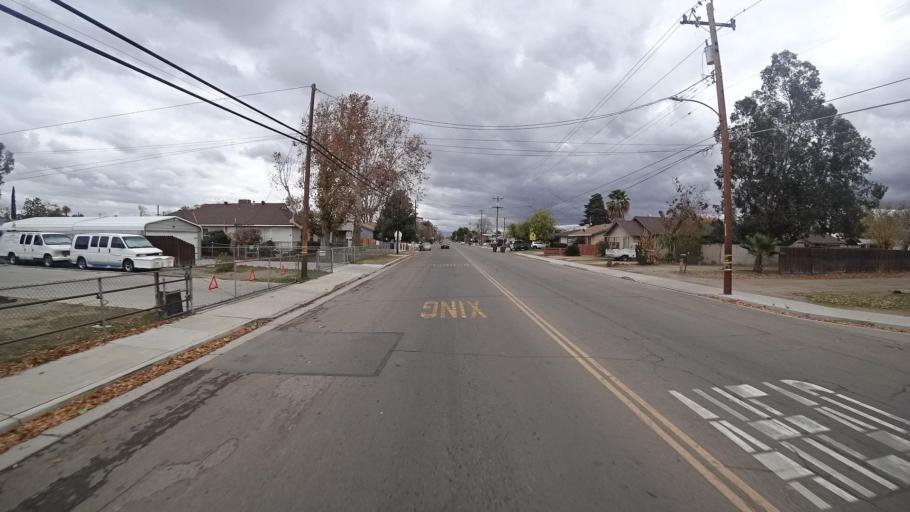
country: US
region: California
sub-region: Kern County
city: Bakersfield
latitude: 35.3467
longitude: -119.0302
